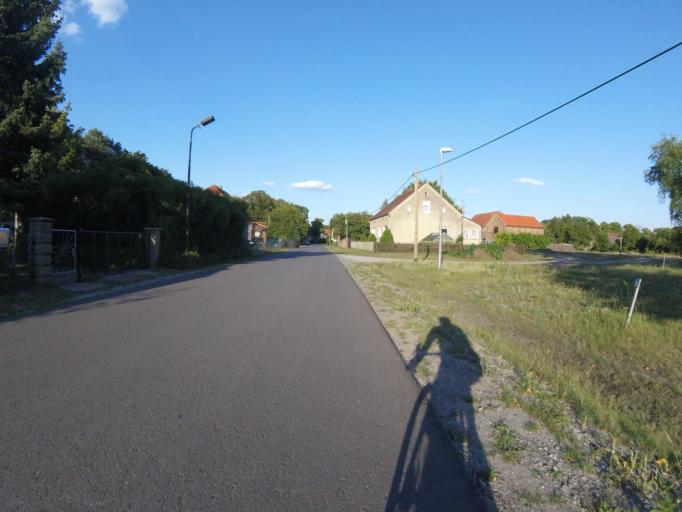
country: DE
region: Brandenburg
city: Gross Koris
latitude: 52.1709
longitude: 13.6552
